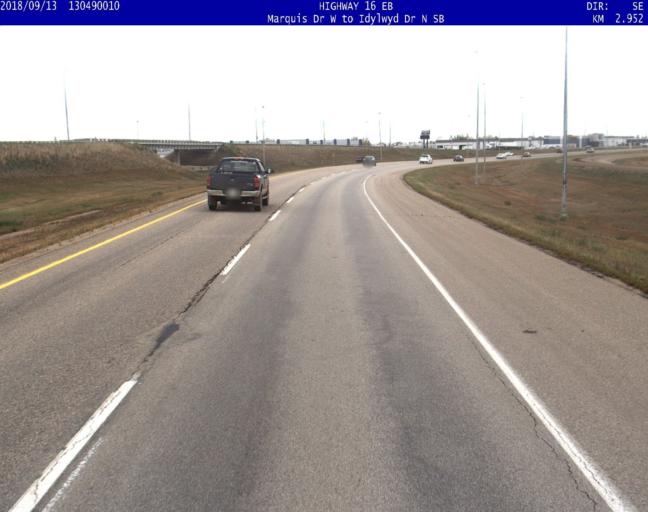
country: CA
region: Saskatchewan
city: Saskatoon
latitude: 52.1837
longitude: -106.6739
